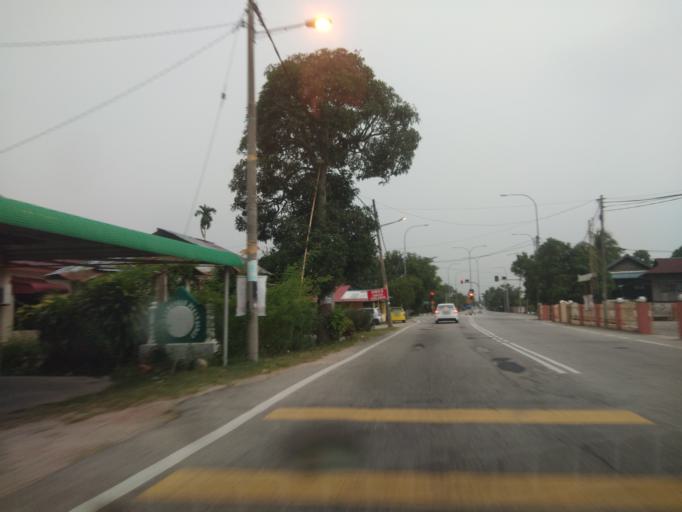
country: MY
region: Penang
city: Permatang Kuching
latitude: 5.4745
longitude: 100.4013
